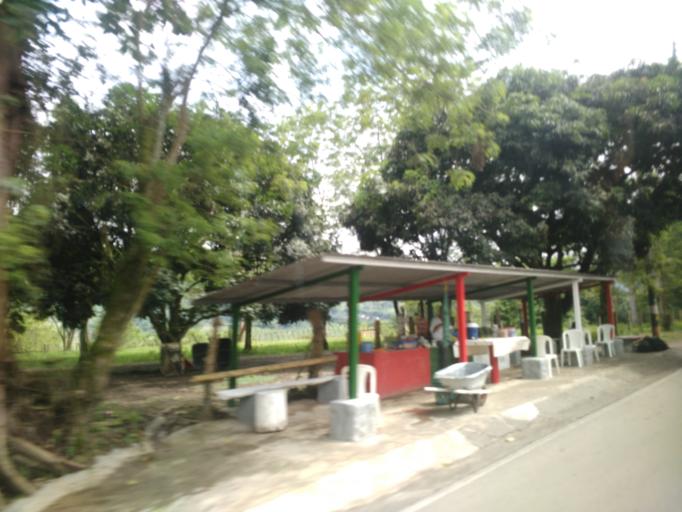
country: CO
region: Valle del Cauca
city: Caicedonia
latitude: 4.3374
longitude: -75.8589
